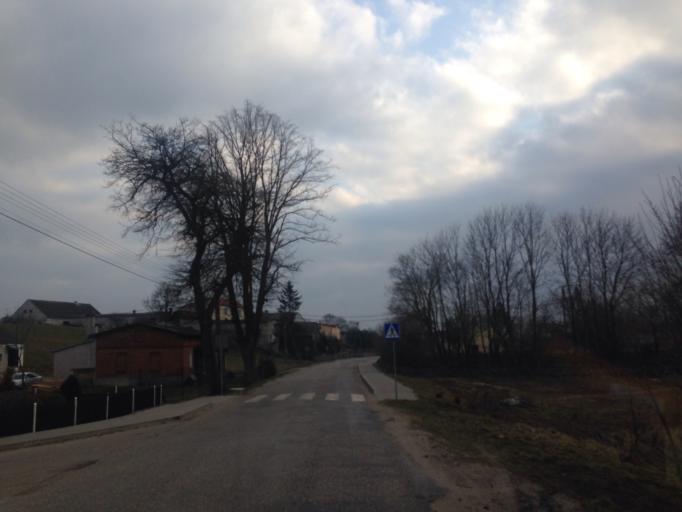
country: PL
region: Kujawsko-Pomorskie
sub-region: Powiat brodnicki
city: Brzozie
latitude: 53.3271
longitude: 19.7188
